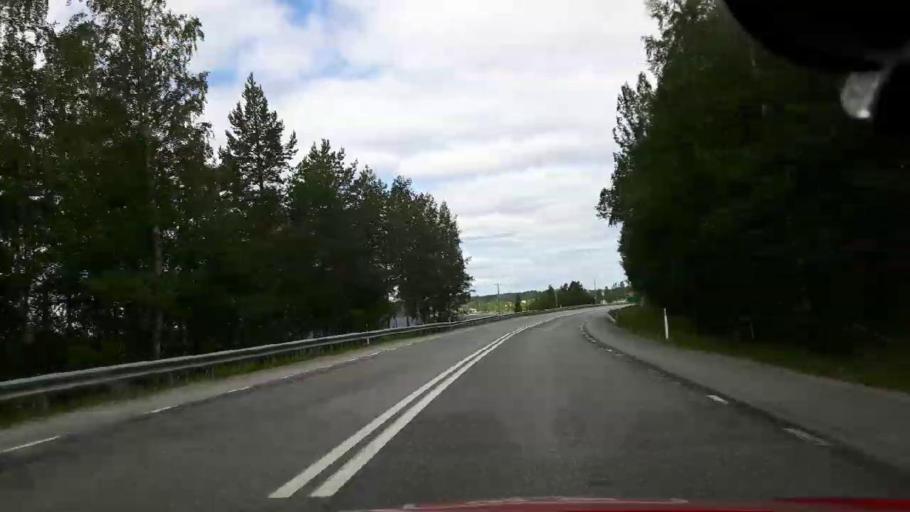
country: SE
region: Jaemtland
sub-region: Braecke Kommun
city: Braecke
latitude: 62.7399
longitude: 15.4278
